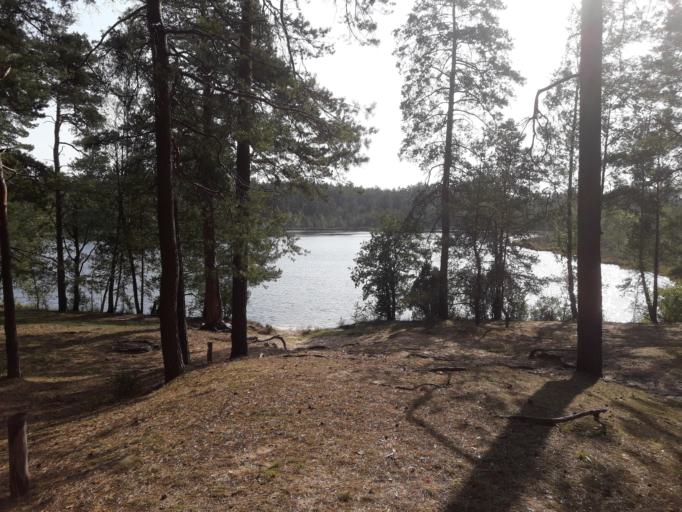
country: LT
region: Alytaus apskritis
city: Druskininkai
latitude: 54.0083
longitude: 24.0897
